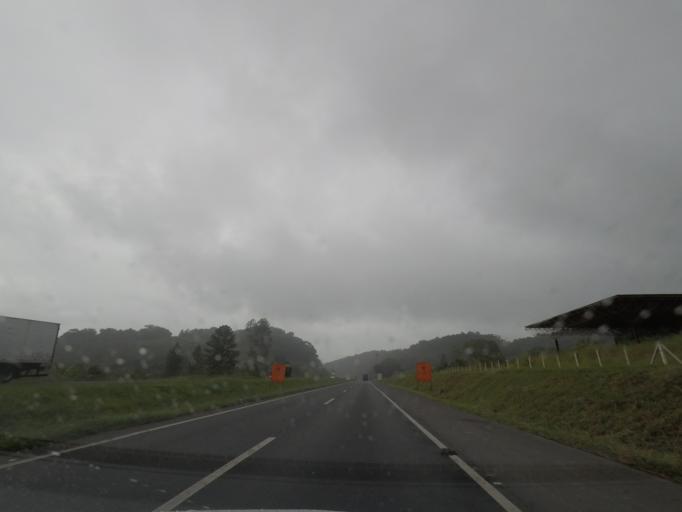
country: BR
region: Sao Paulo
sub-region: Juquia
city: Juquia
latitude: -24.3963
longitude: -47.7280
